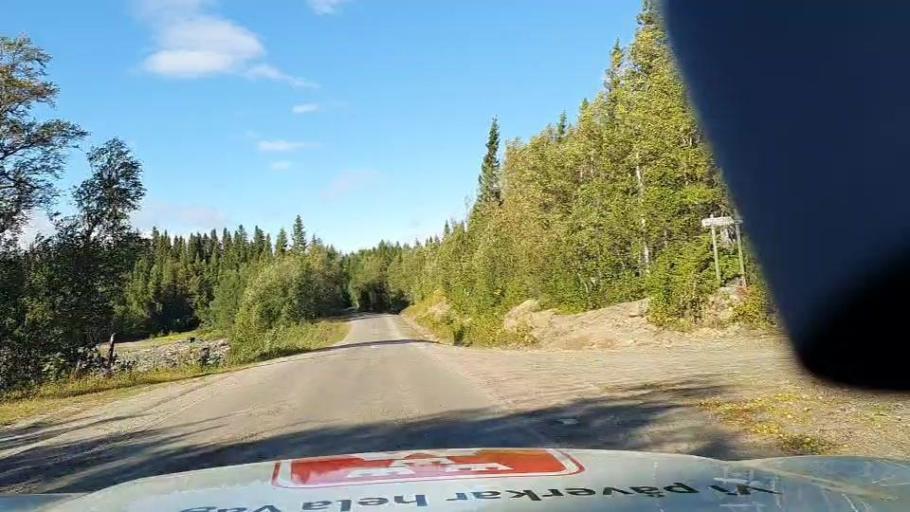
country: SE
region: Jaemtland
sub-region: Stroemsunds Kommun
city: Stroemsund
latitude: 64.5425
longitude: 15.0879
